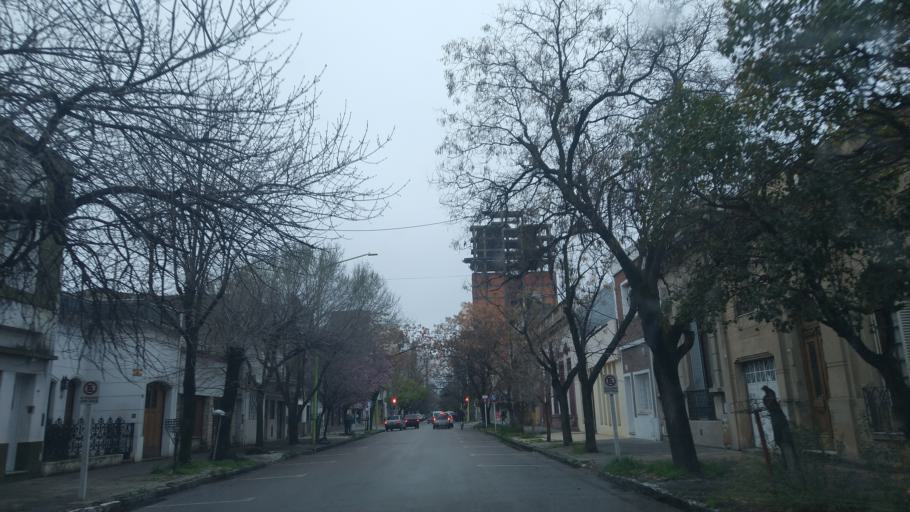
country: AR
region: Buenos Aires
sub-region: Partido de Bahia Blanca
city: Bahia Blanca
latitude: -38.7172
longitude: -62.2735
